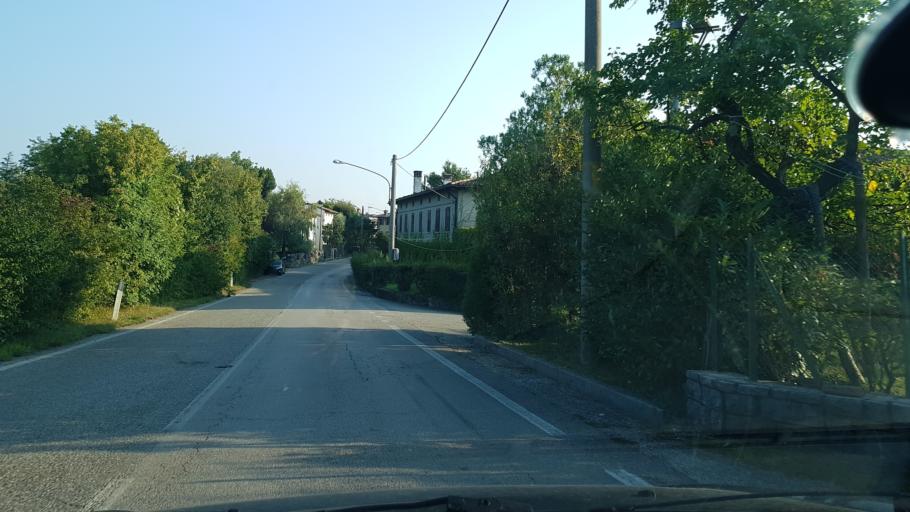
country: IT
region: Friuli Venezia Giulia
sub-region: Provincia di Gorizia
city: San Floriano del Collio
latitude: 45.9735
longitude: 13.6119
